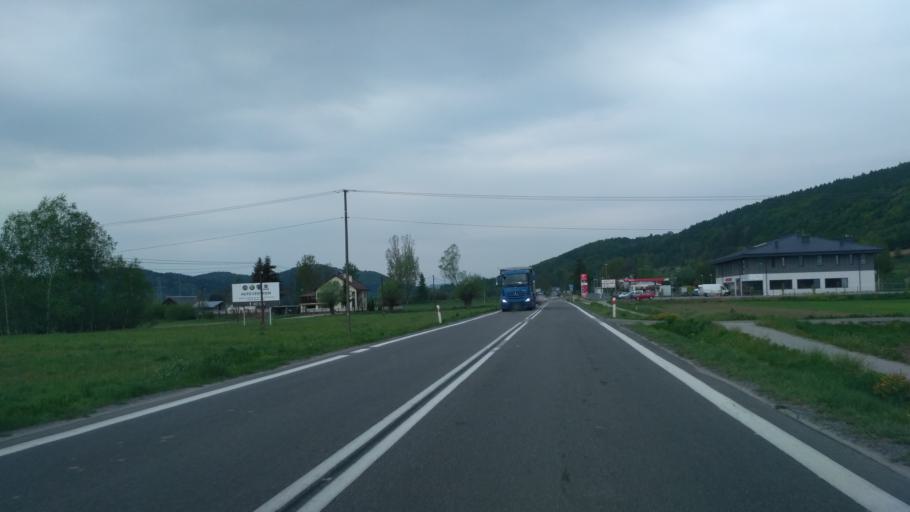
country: PL
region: Subcarpathian Voivodeship
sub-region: Powiat debicki
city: Brzostek
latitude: 49.8950
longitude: 21.3826
